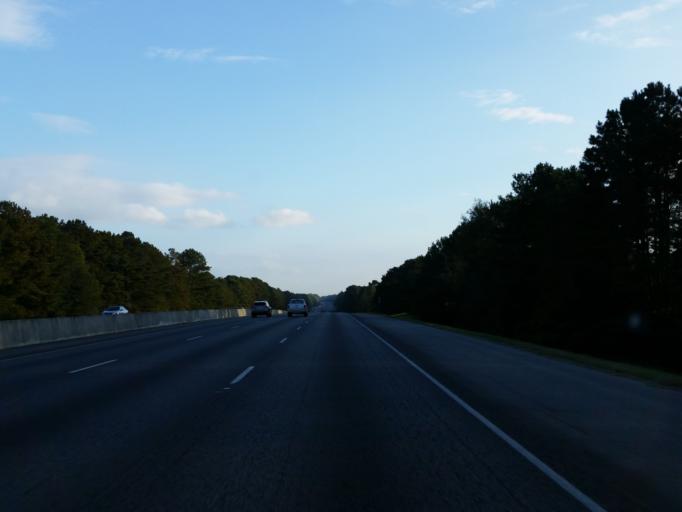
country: US
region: Georgia
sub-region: Bibb County
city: West Point
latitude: 32.9307
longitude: -83.8050
